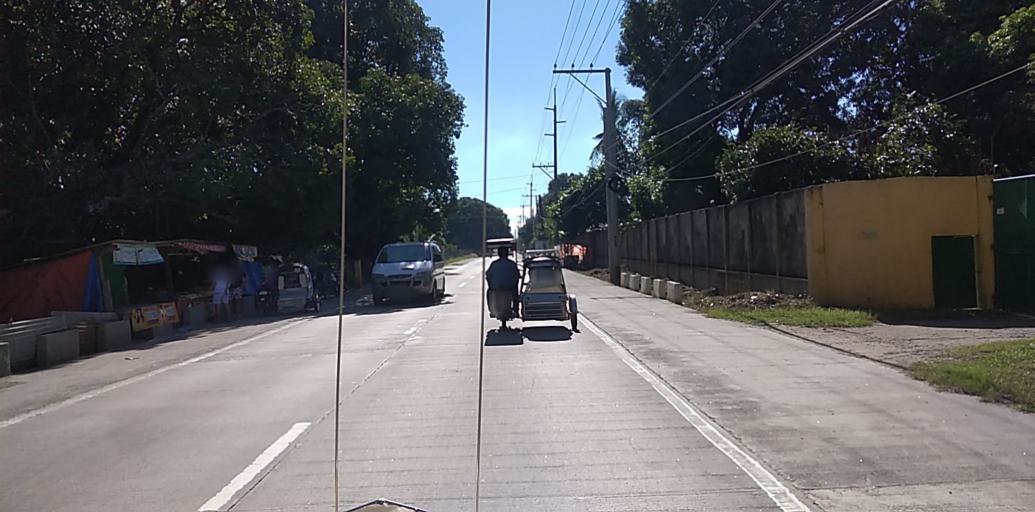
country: PH
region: Central Luzon
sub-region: Province of Pampanga
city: Santo Domingo
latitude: 15.0659
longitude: 120.7678
